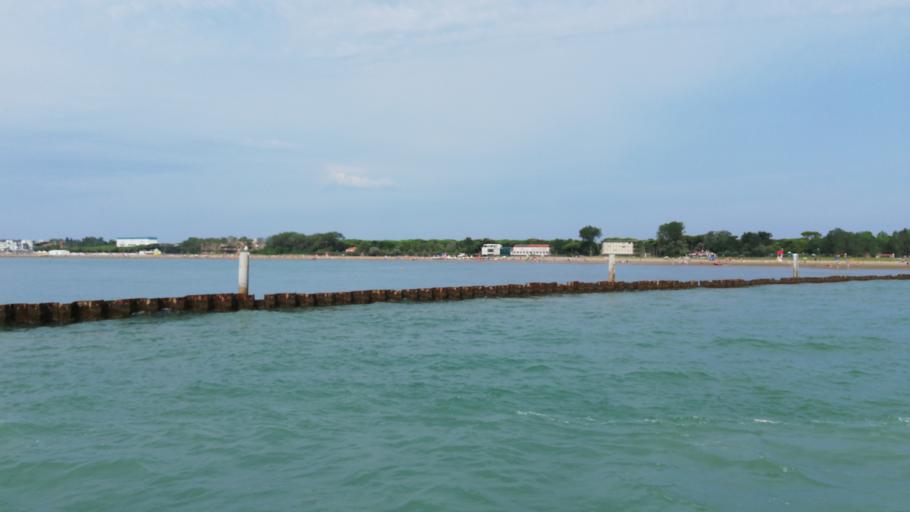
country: IT
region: Veneto
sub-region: Provincia di Venezia
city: Caorle
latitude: 45.6120
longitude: 12.9127
